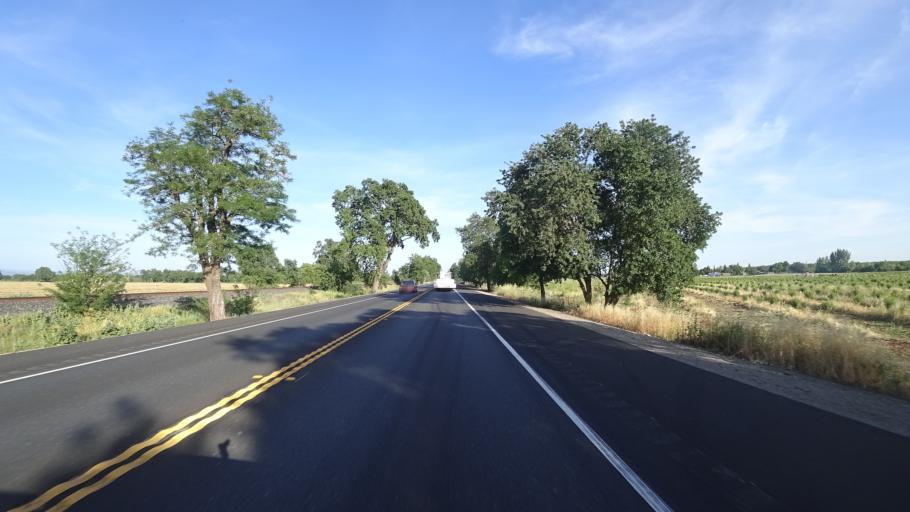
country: US
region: California
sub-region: Yuba County
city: Wheatland
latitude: 39.0202
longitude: -121.4411
